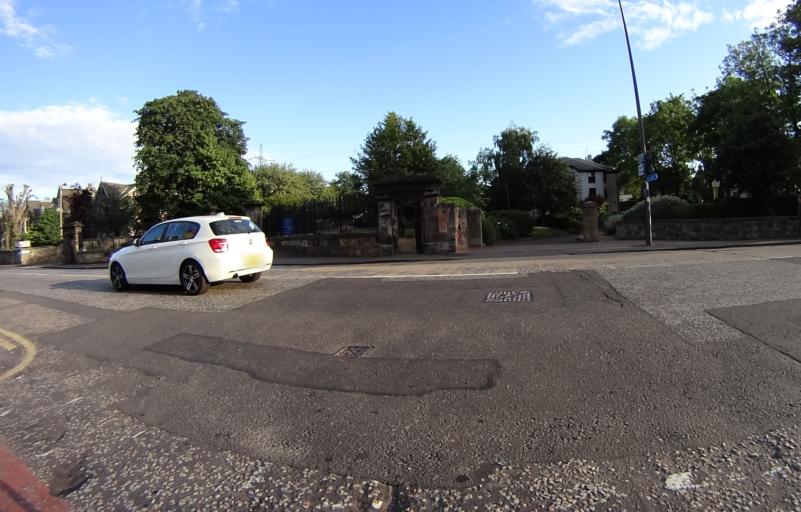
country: GB
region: Scotland
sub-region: West Lothian
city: Seafield
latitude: 55.9514
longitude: -3.1087
